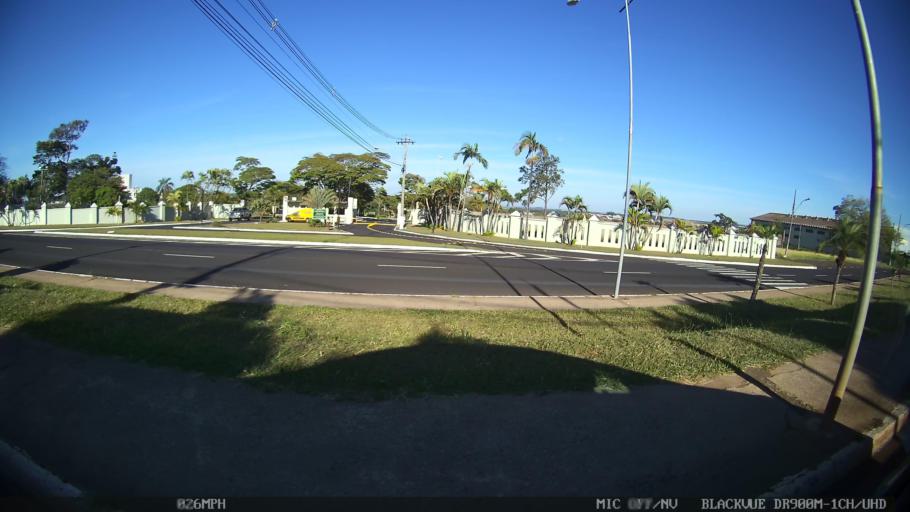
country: BR
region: Sao Paulo
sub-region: Franca
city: Franca
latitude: -20.5734
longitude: -47.3902
